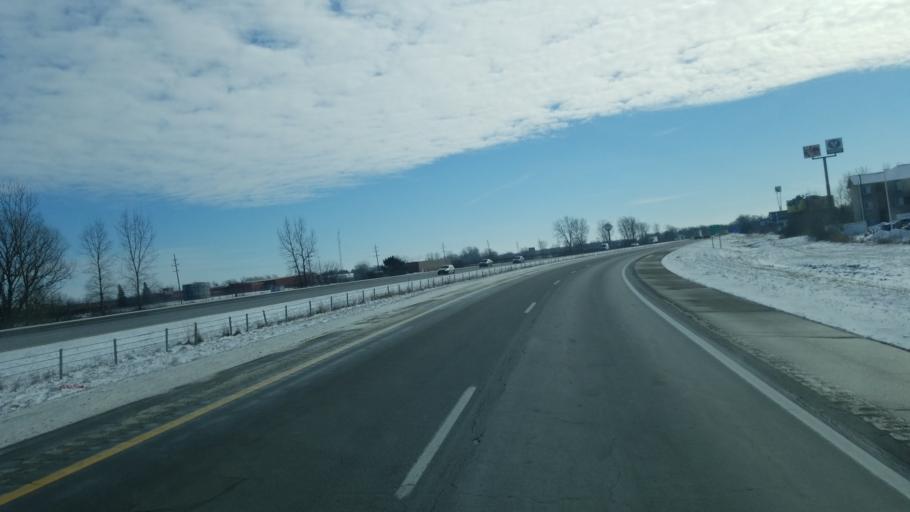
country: US
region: Michigan
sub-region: Washtenaw County
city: Milan
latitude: 42.0983
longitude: -83.6752
